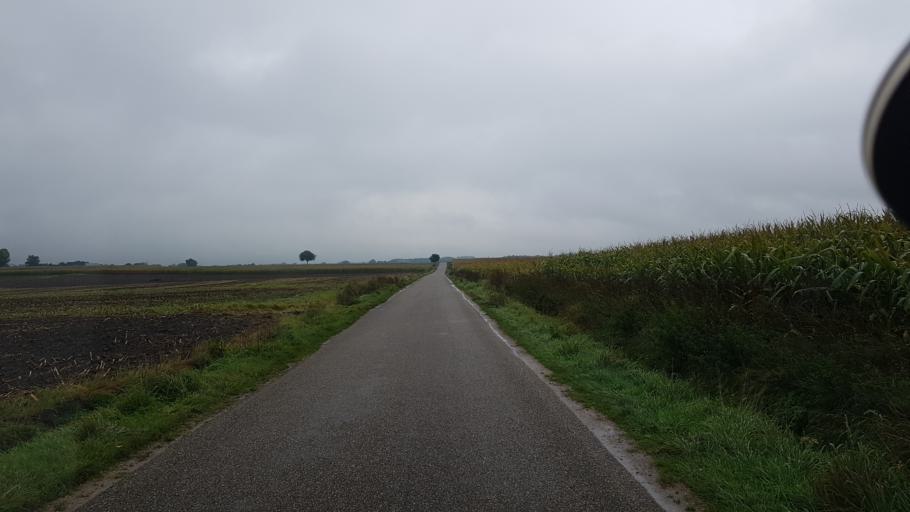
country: NL
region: Gelderland
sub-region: Gemeente Apeldoorn
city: Beekbergen
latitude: 52.1573
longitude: 5.9772
